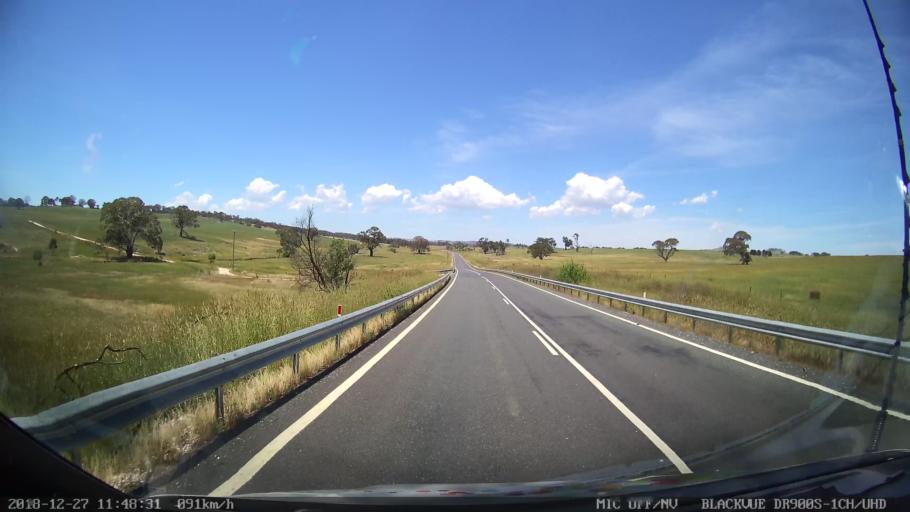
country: AU
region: New South Wales
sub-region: Bathurst Regional
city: Perthville
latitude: -33.6073
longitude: 149.4358
